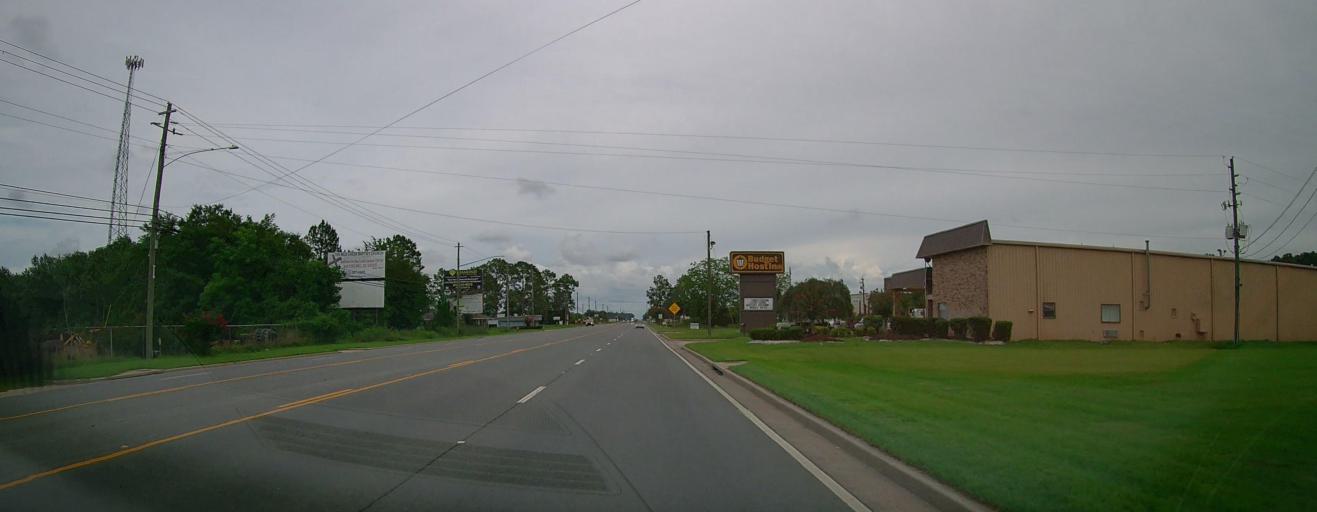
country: US
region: Georgia
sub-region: Appling County
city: Baxley
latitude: 31.7738
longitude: -82.3346
